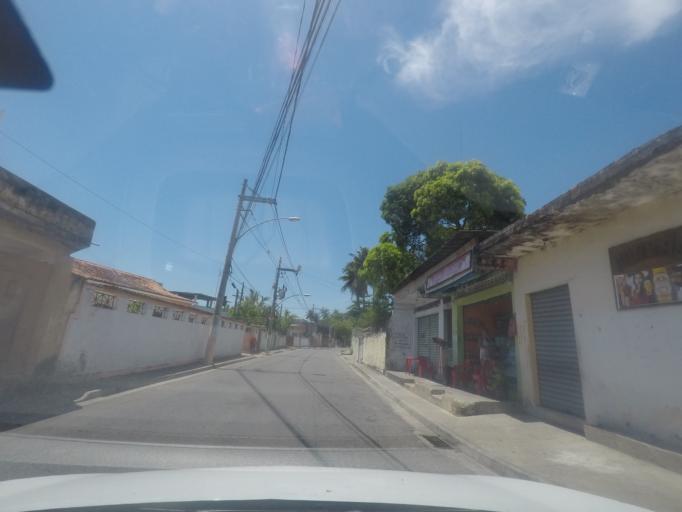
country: BR
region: Rio de Janeiro
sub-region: Itaguai
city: Itaguai
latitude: -22.9836
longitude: -43.6850
